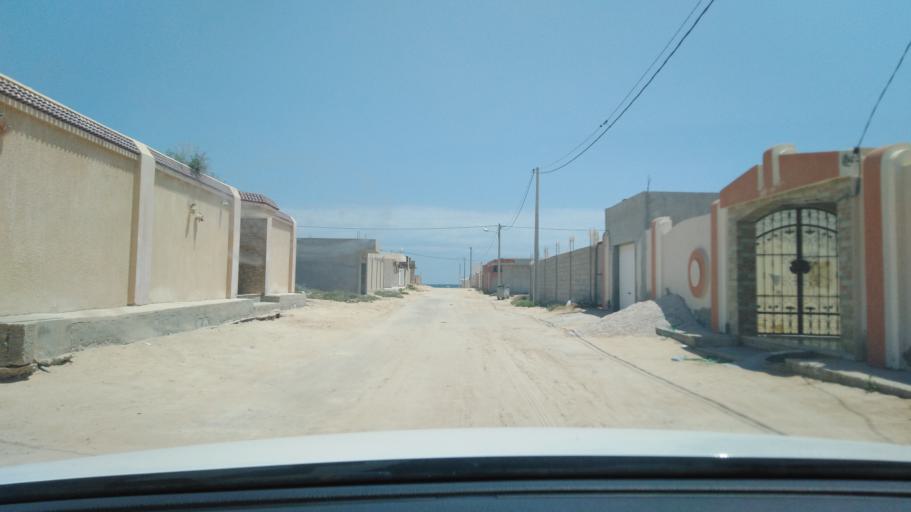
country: TN
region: Qabis
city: Gabes
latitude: 33.9474
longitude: 10.0721
